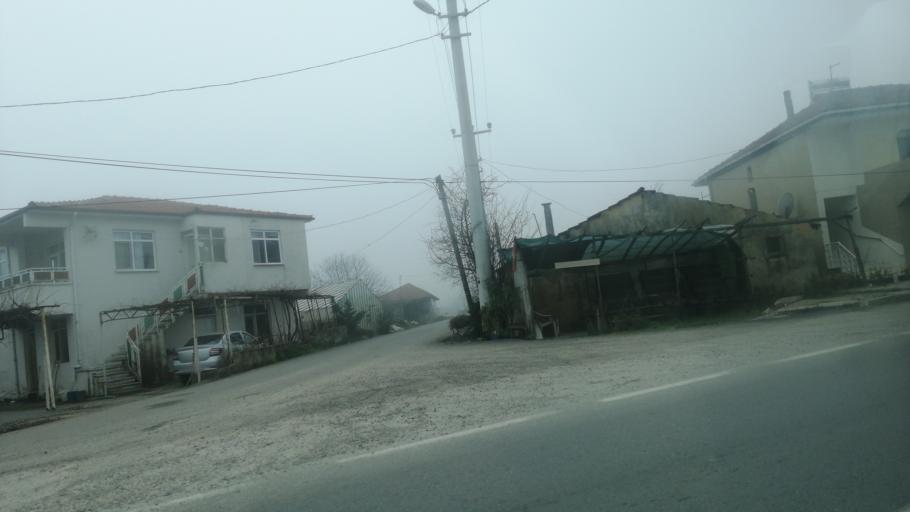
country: TR
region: Yalova
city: Korukoy
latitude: 40.6521
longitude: 29.1845
